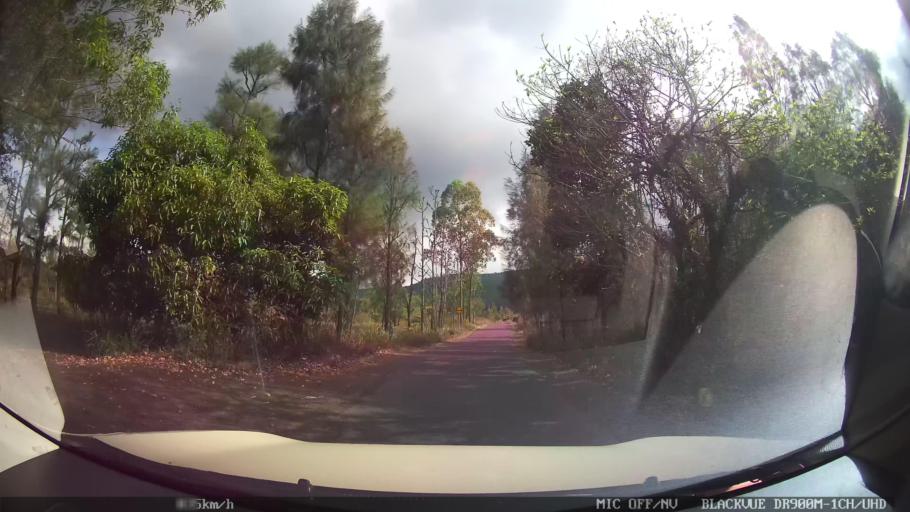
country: ID
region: Bali
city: Banjar Kedisan
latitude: -8.2367
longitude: 115.3543
